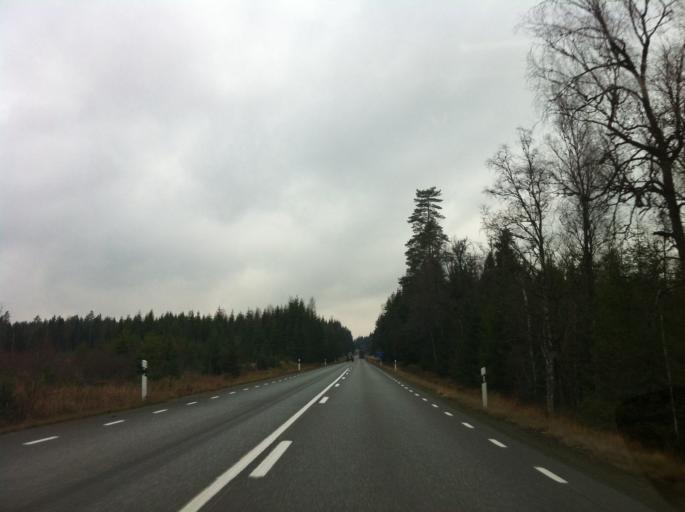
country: SE
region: Joenkoeping
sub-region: Vetlanda Kommun
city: Landsbro
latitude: 57.3945
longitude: 14.8427
